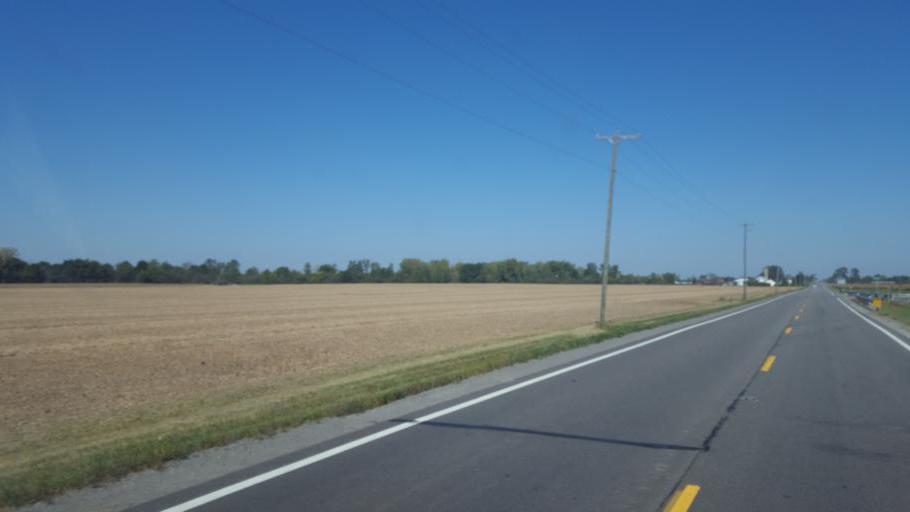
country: US
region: Ohio
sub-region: Marion County
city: Marion
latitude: 40.5999
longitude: -83.0347
